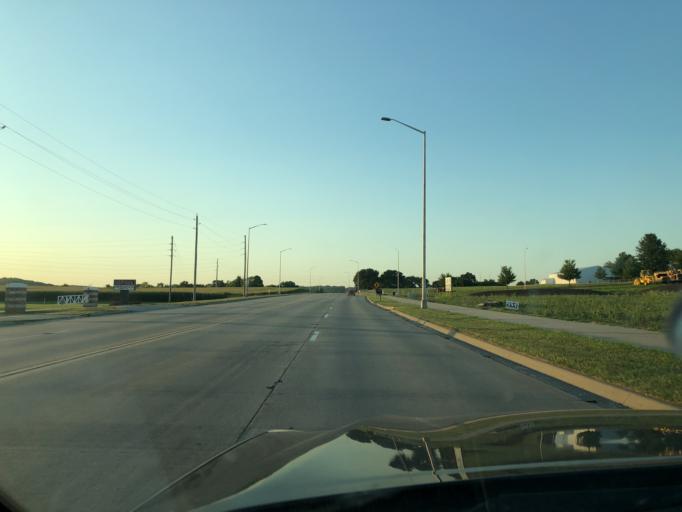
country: US
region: Kansas
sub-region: Leavenworth County
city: Leavenworth
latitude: 39.2695
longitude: -94.9468
